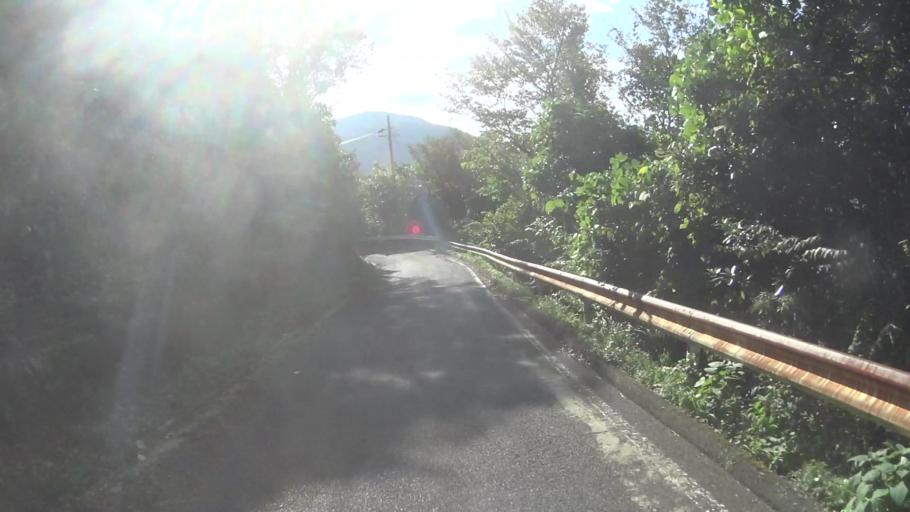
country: JP
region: Kyoto
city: Maizuru
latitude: 35.5650
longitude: 135.4099
